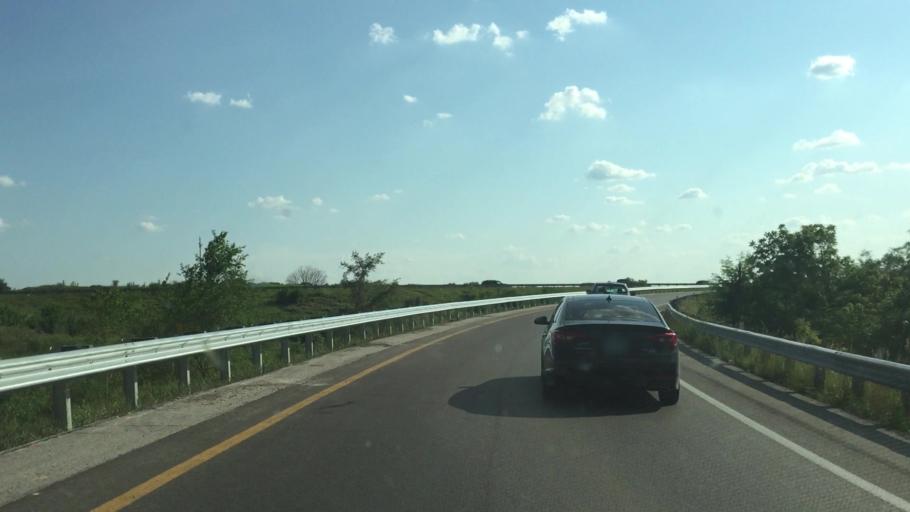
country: US
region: Missouri
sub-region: Platte County
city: Riverside
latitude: 39.1860
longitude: -94.5923
